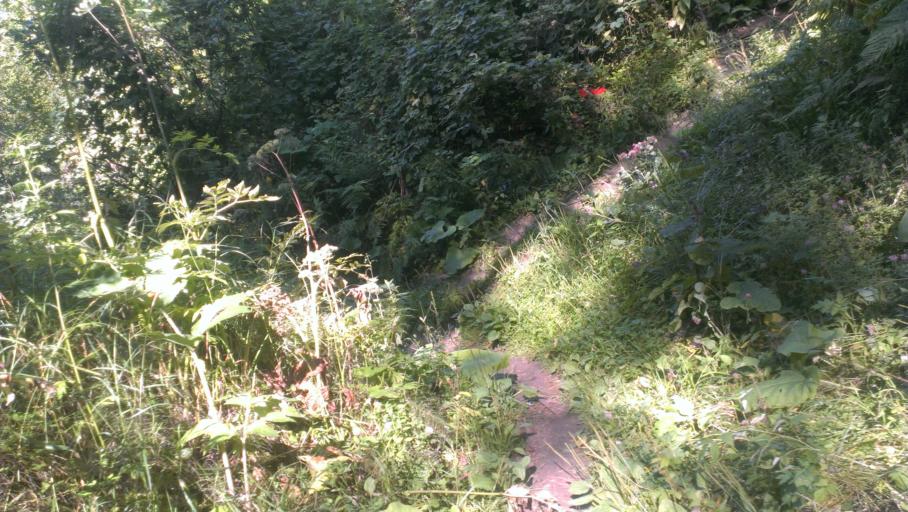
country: RU
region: Altai Krai
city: Nauchnyy Gorodok
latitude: 53.4250
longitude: 83.5050
